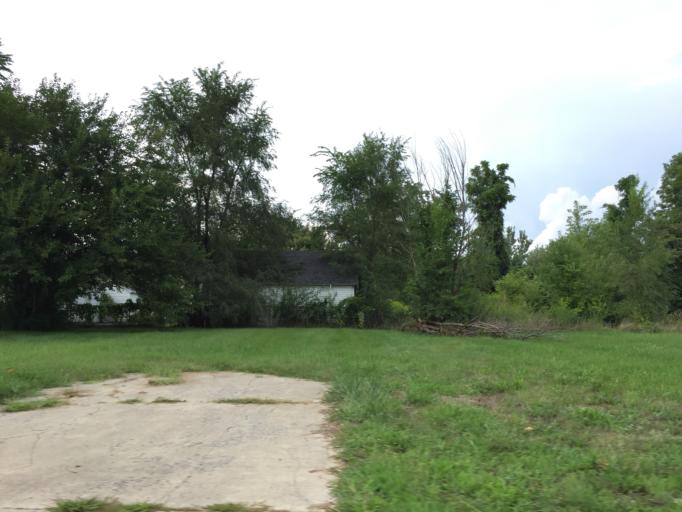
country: US
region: Indiana
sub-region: Howard County
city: Kokomo
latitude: 40.4718
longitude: -86.1152
